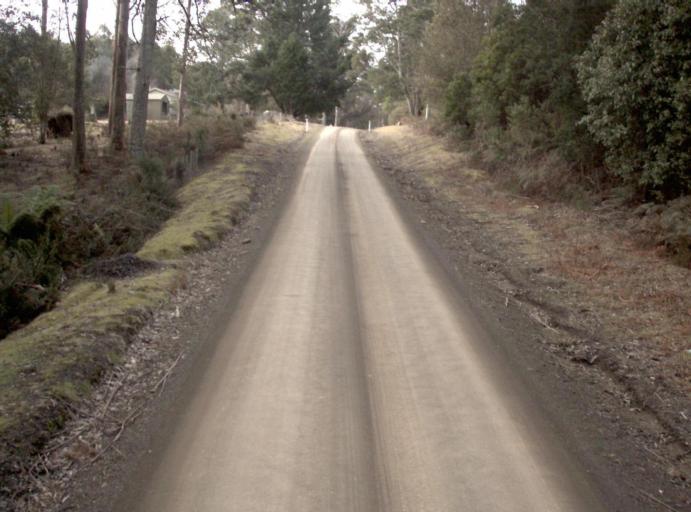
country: AU
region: Tasmania
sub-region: Dorset
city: Scottsdale
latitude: -41.2758
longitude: 147.3427
